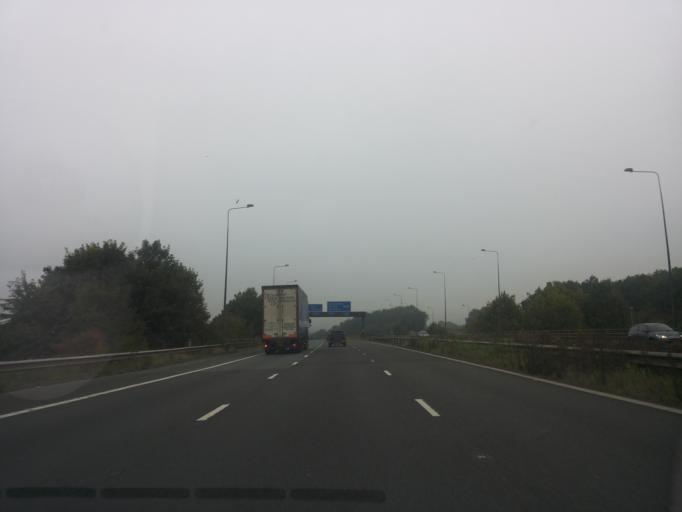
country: GB
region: England
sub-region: Borough of Bury
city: Bury
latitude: 53.5780
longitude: -2.2715
